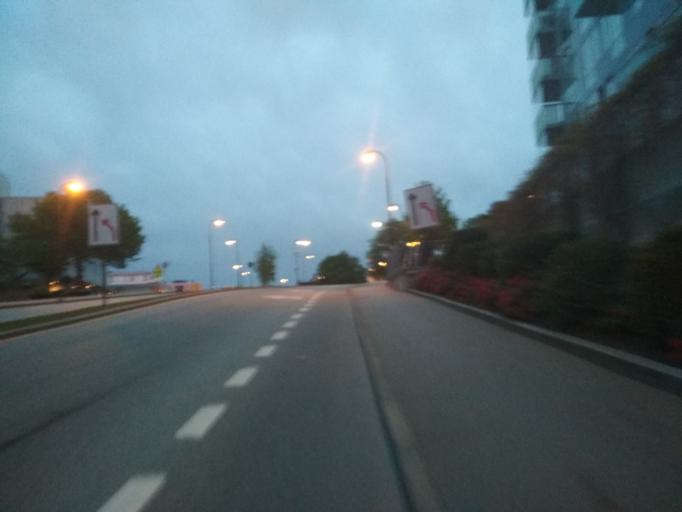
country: NO
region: Rogaland
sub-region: Stavanger
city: Stavanger
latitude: 58.9728
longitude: 5.7221
